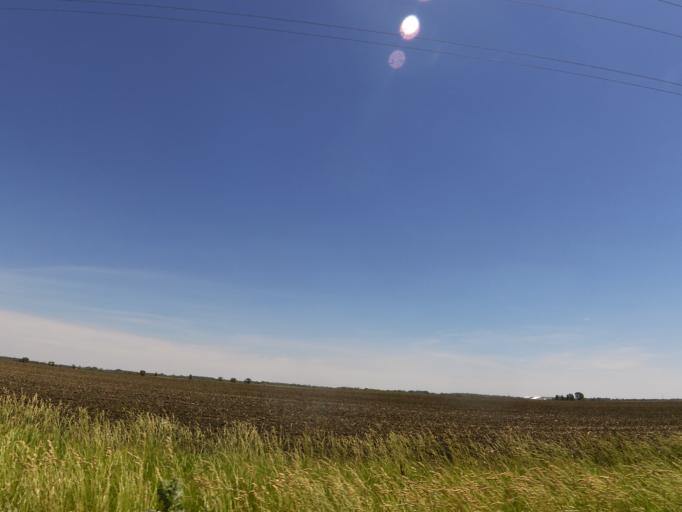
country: US
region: Illinois
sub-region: Iroquois County
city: Milford
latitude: 40.6355
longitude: -87.7529
